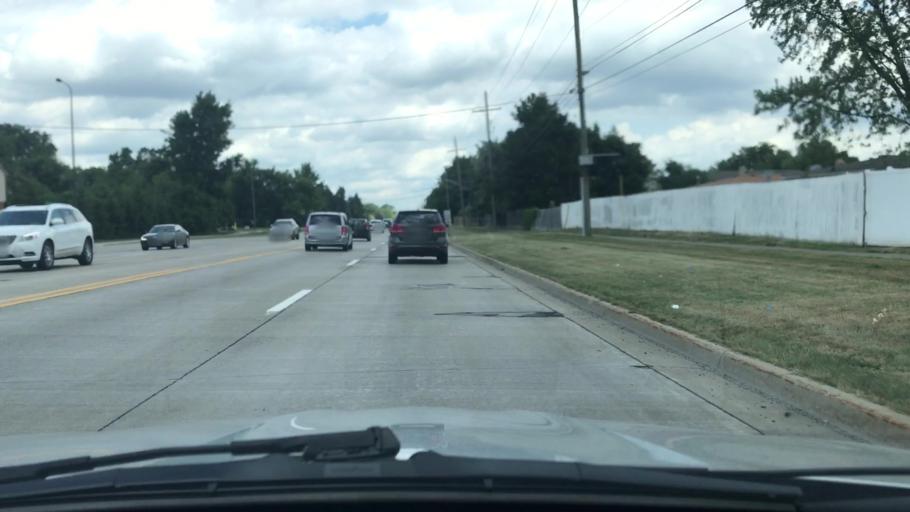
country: US
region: Michigan
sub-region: Macomb County
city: Sterling Heights
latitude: 42.5712
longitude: -83.0890
